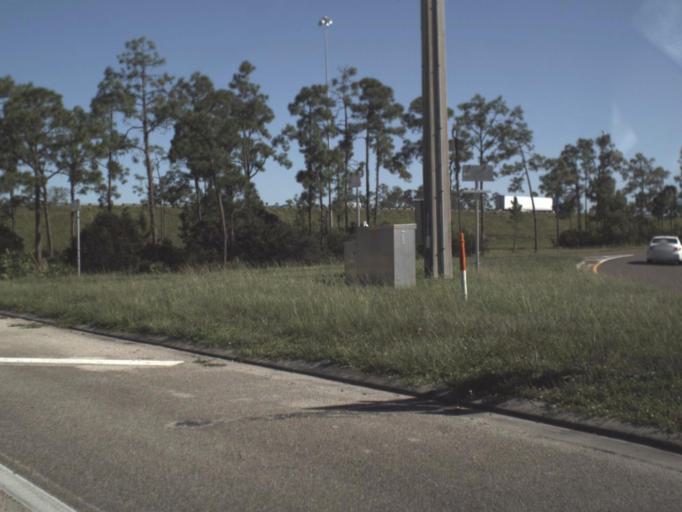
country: US
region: Florida
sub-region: Lee County
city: Gateway
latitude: 26.5472
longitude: -81.7968
